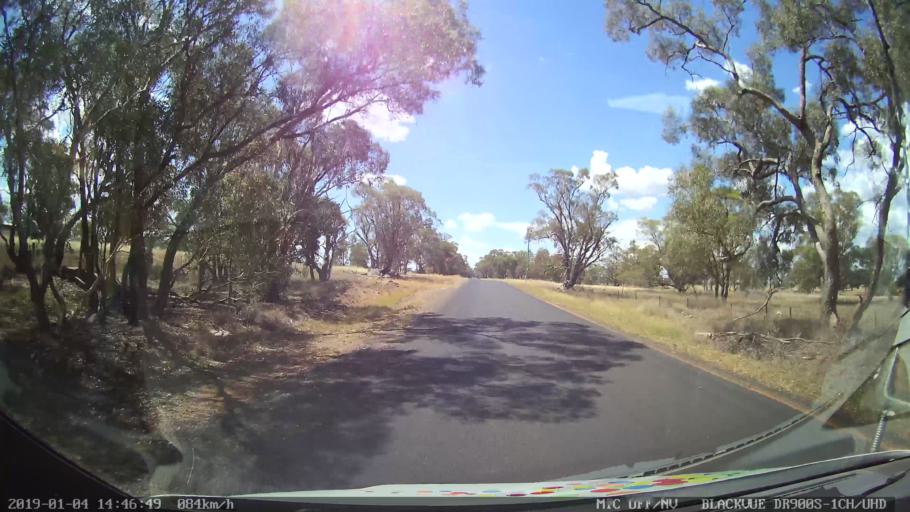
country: AU
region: New South Wales
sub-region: Dubbo Municipality
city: Dubbo
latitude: -32.0767
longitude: 148.6590
